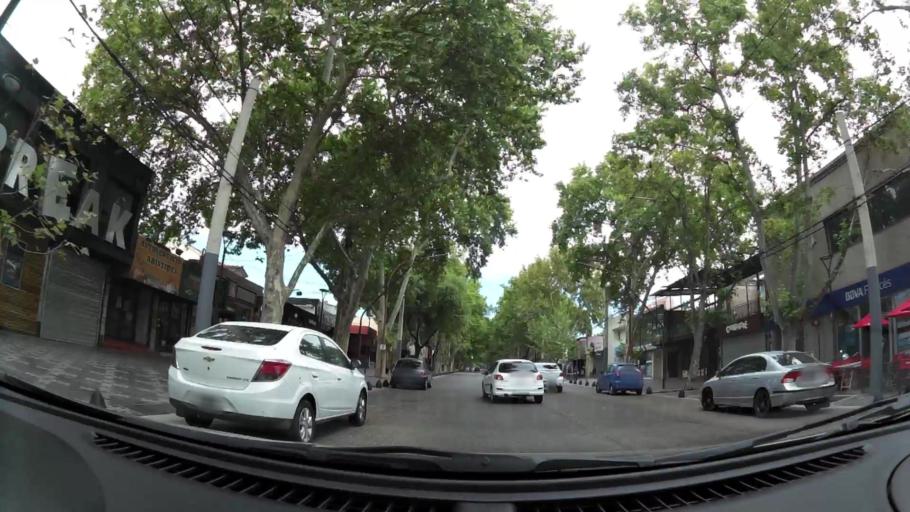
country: AR
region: Mendoza
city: Mendoza
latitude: -32.8923
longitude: -68.8551
